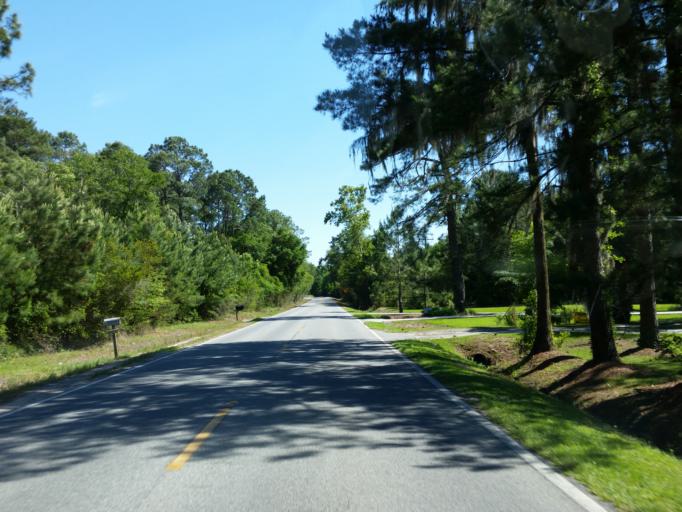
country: US
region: Georgia
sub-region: Cook County
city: Adel
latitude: 31.1120
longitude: -83.4142
